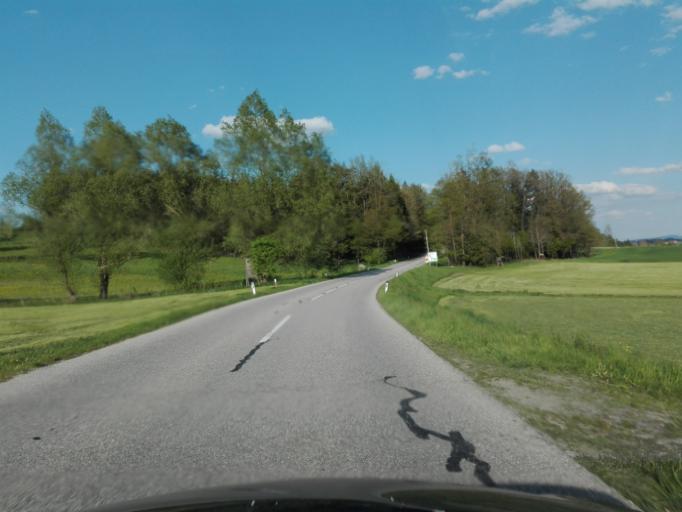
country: AT
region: Upper Austria
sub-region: Politischer Bezirk Rohrbach
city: Atzesberg
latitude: 48.4759
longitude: 13.9572
